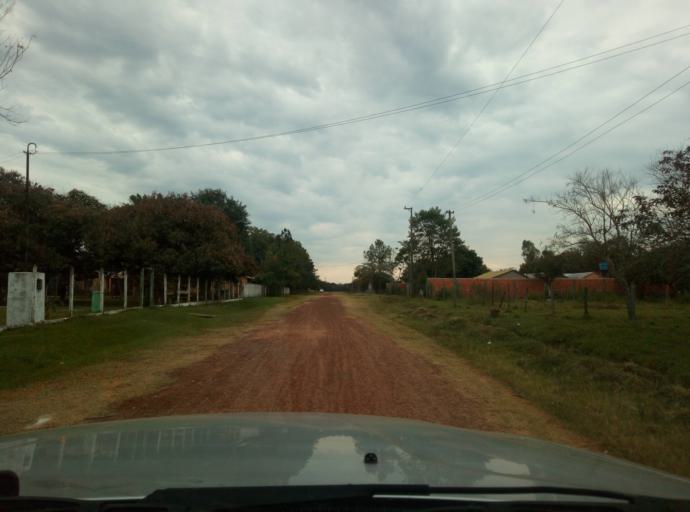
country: PY
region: Caaguazu
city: Carayao
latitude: -25.1536
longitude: -56.3338
